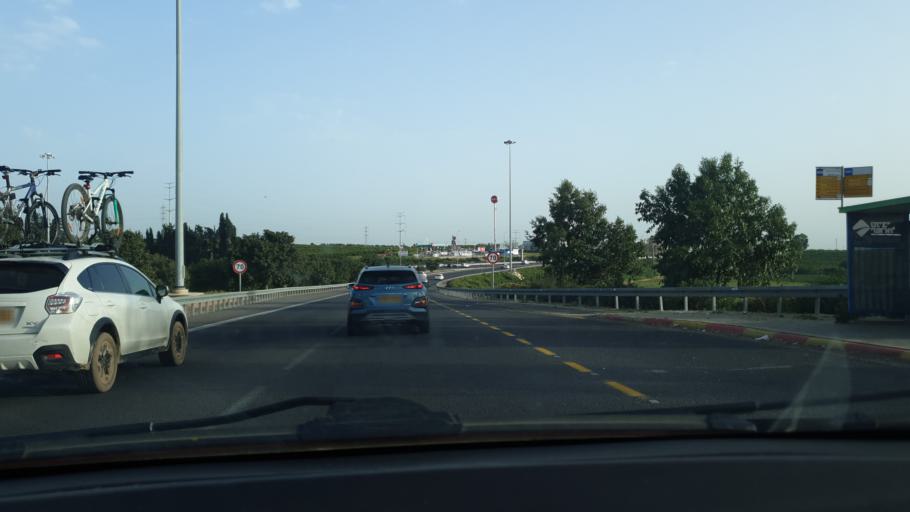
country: IL
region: Central District
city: Even Yehuda
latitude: 32.2542
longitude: 34.8892
